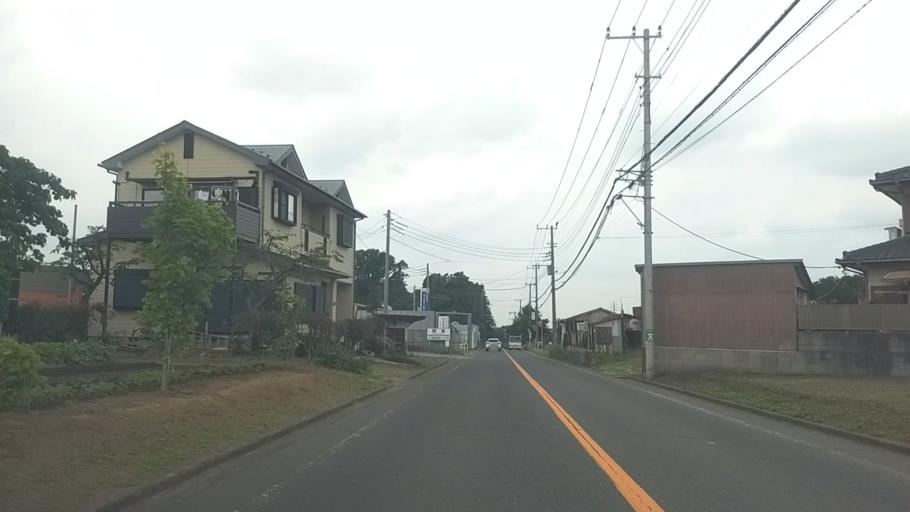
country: JP
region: Kanagawa
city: Fujisawa
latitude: 35.3527
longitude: 139.4352
